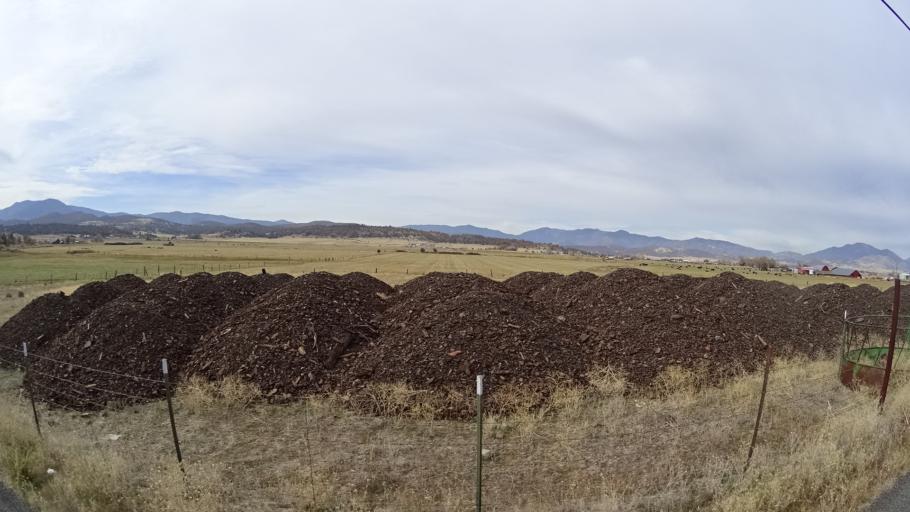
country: US
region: California
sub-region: Siskiyou County
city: Montague
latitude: 41.7026
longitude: -122.5492
